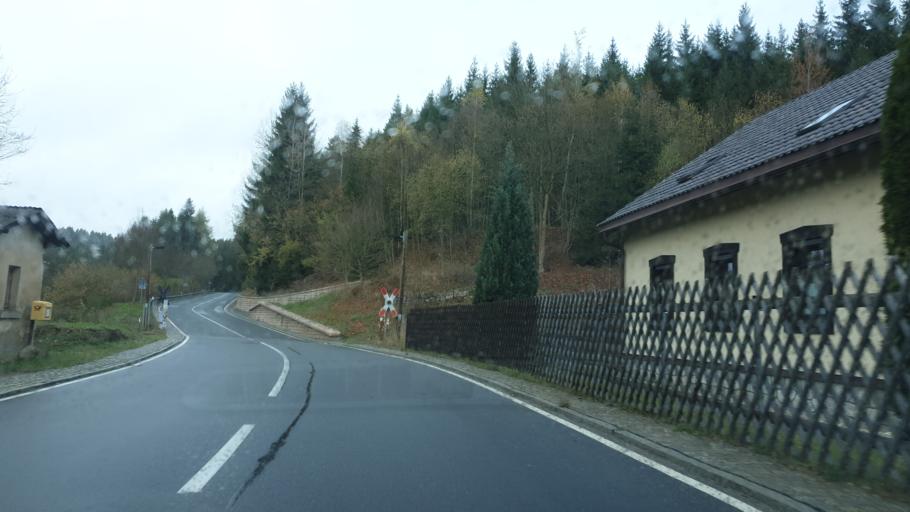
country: DE
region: Saxony
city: Schoenheide
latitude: 50.4807
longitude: 12.5306
